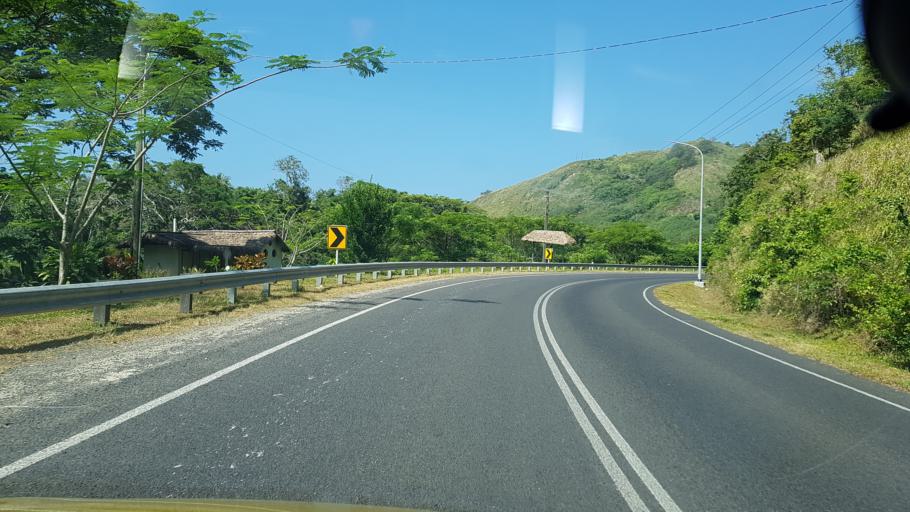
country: FJ
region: Western
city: Nadi
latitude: -18.1741
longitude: 177.5926
